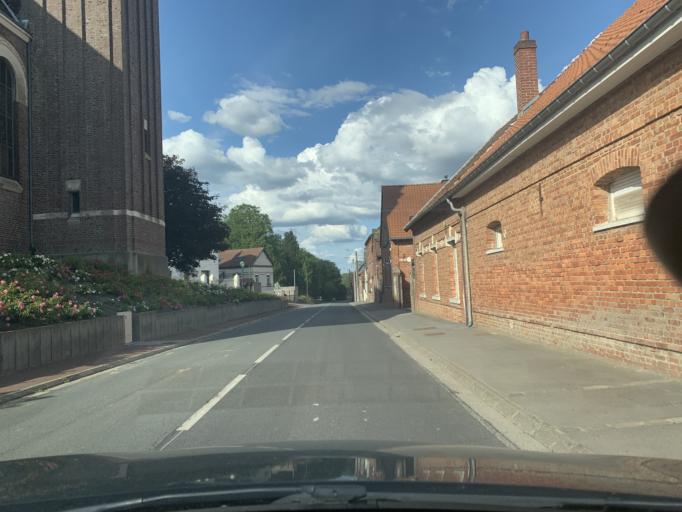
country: FR
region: Nord-Pas-de-Calais
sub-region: Departement du Nord
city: Gouzeaucourt
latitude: 50.0792
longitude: 3.1342
